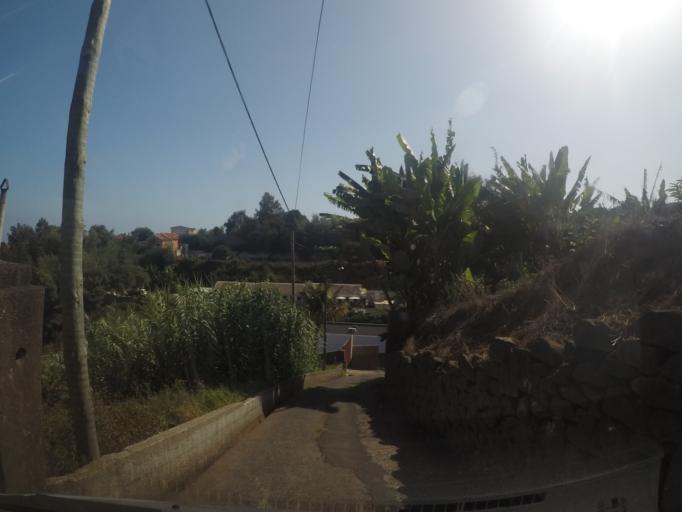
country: PT
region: Madeira
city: Camara de Lobos
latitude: 32.6745
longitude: -16.9461
